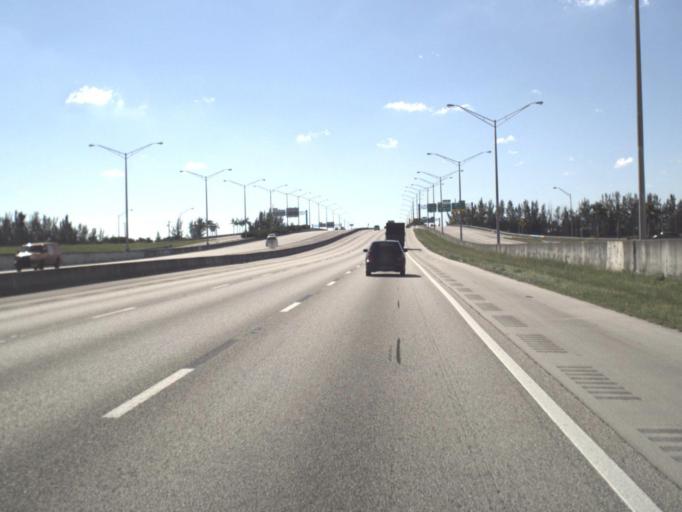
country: US
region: Florida
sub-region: Miami-Dade County
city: Sweetwater
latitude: 25.7875
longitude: -80.3861
